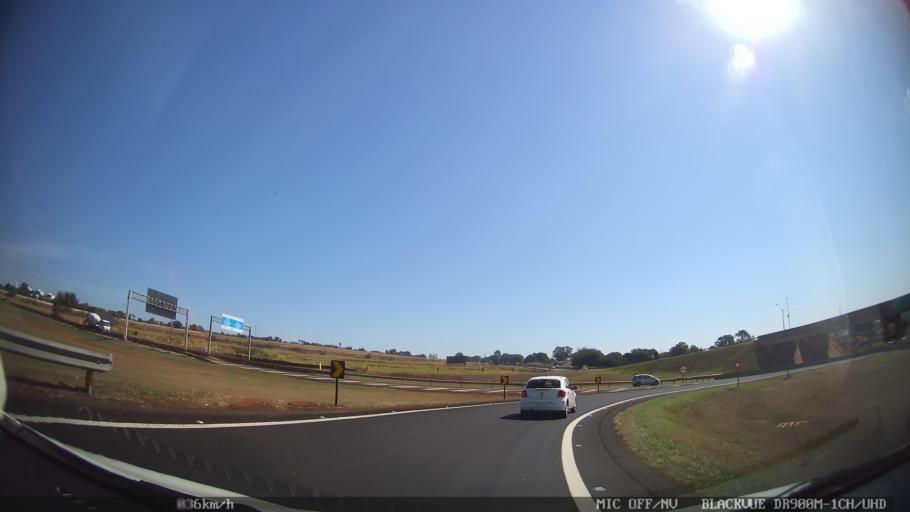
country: BR
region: Sao Paulo
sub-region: Ribeirao Preto
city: Ribeirao Preto
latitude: -21.2235
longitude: -47.7763
